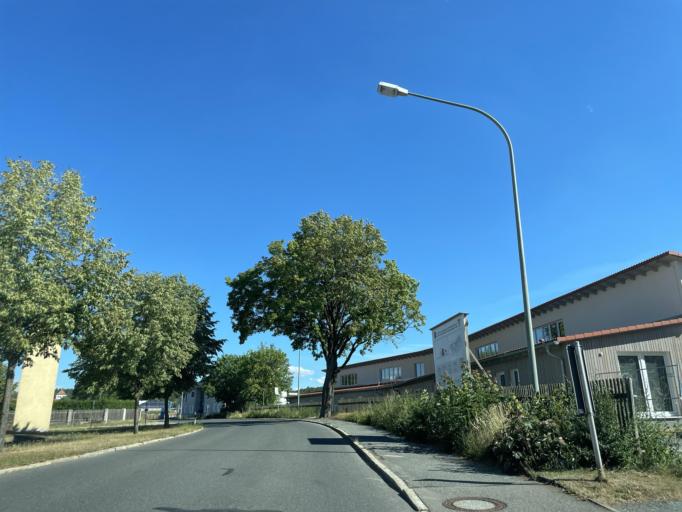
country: DE
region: Bavaria
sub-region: Upper Palatinate
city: Trabitz
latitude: 49.8007
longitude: 11.8962
